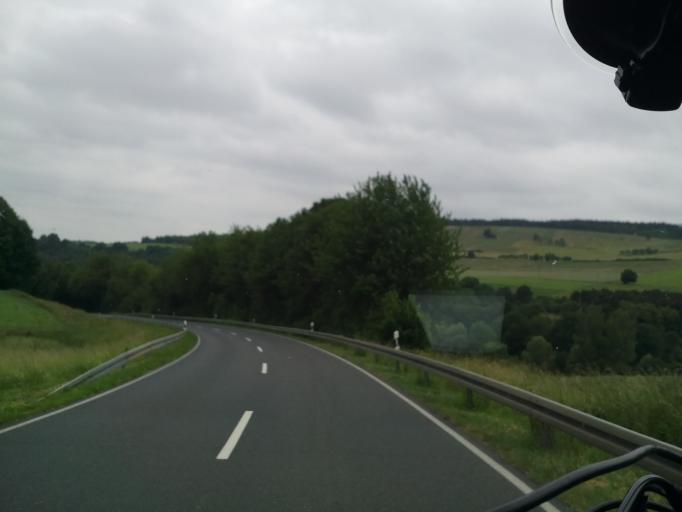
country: DE
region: Bavaria
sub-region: Regierungsbezirk Unterfranken
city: Kreuzwertheim
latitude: 49.7452
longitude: 9.5914
